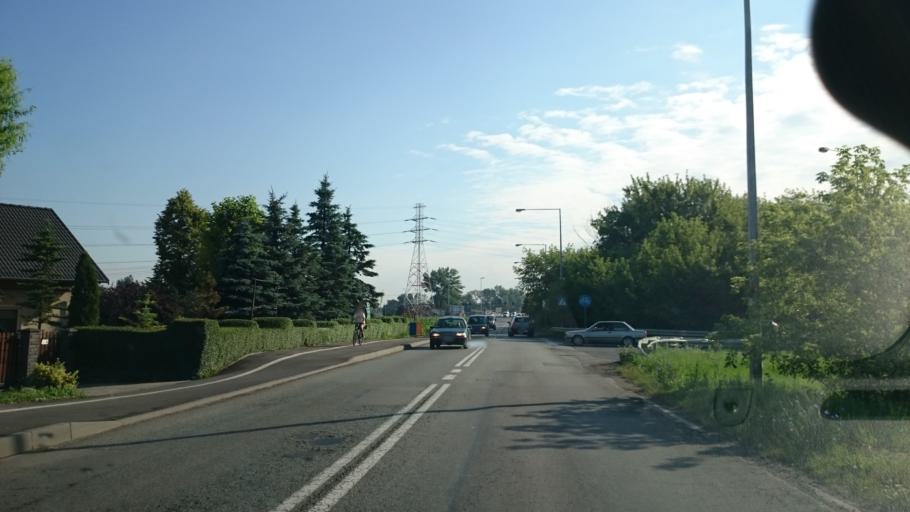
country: PL
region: Opole Voivodeship
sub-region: Powiat opolski
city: Opole
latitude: 50.7013
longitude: 17.9316
